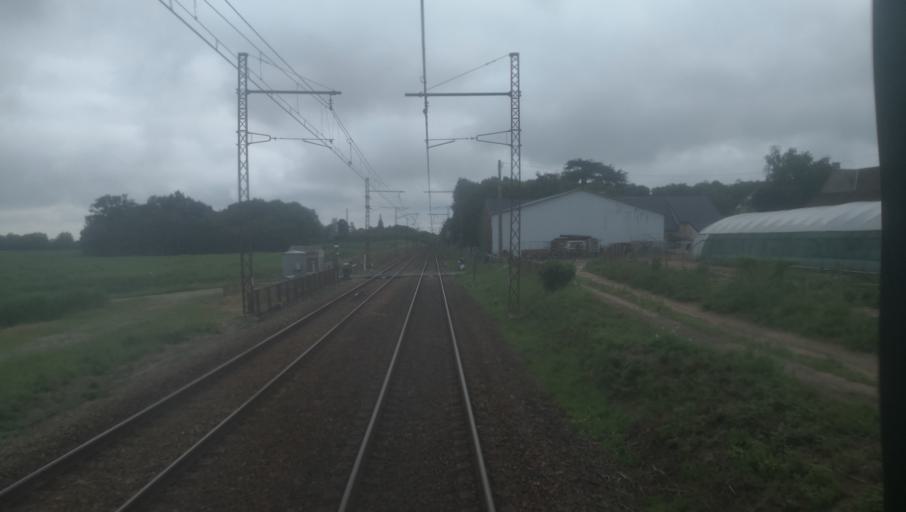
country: FR
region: Centre
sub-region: Departement du Cher
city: Mereau
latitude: 47.1430
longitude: 2.0487
